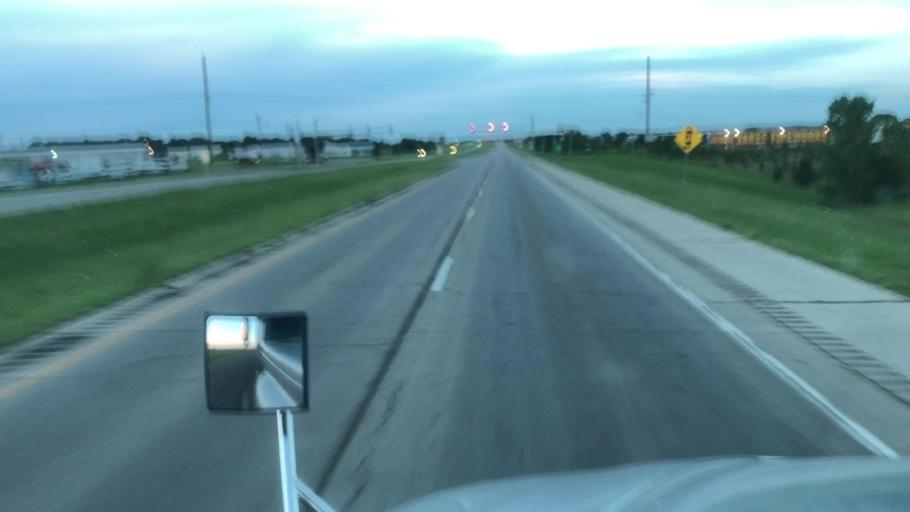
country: US
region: Oklahoma
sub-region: Kay County
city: Ponca City
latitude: 36.7513
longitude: -97.0664
